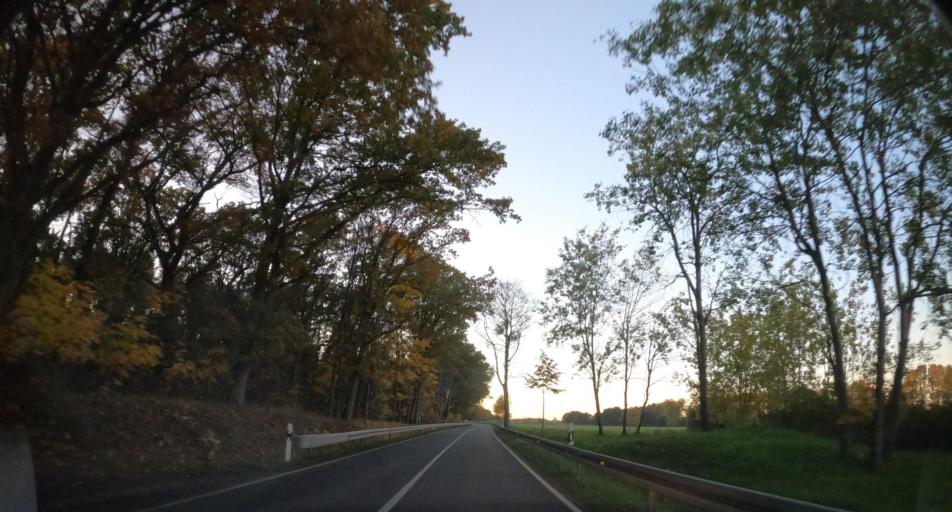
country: DE
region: Mecklenburg-Vorpommern
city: Ueckermunde
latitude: 53.7640
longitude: 13.9938
